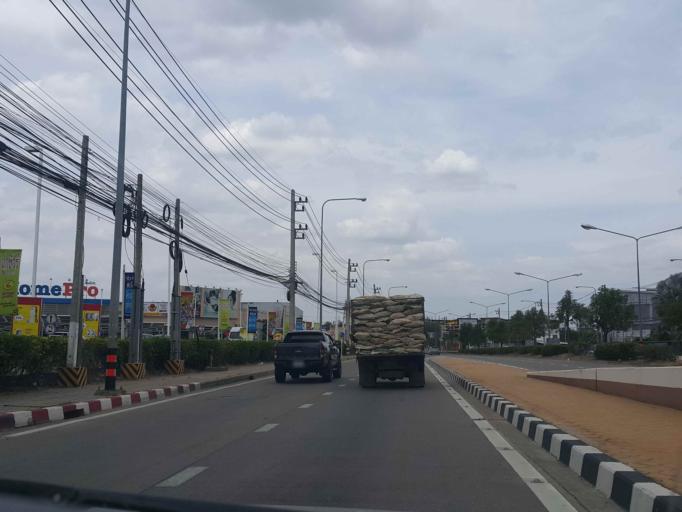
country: TH
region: Chiang Mai
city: Chiang Mai
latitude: 18.7425
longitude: 98.9610
